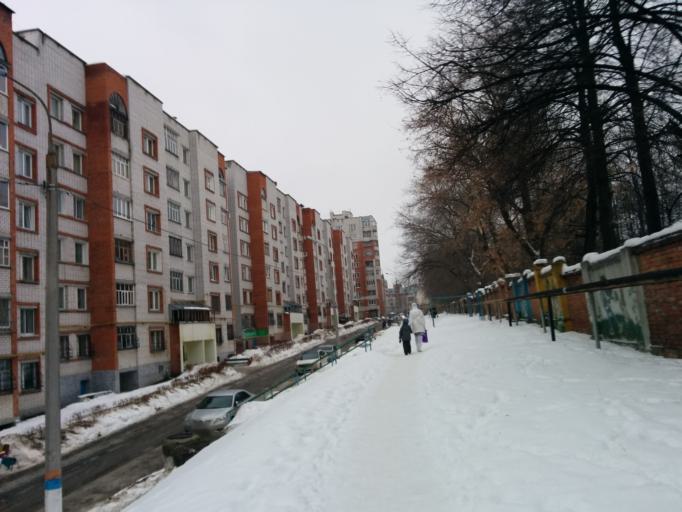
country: RU
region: Chuvashia
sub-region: Cheboksarskiy Rayon
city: Cheboksary
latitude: 56.1442
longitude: 47.2318
